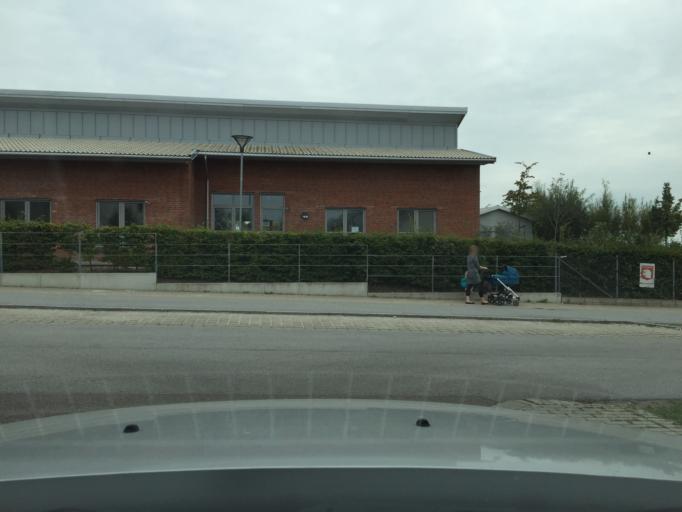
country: SE
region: Skane
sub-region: Lunds Kommun
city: Lund
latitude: 55.6926
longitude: 13.2354
